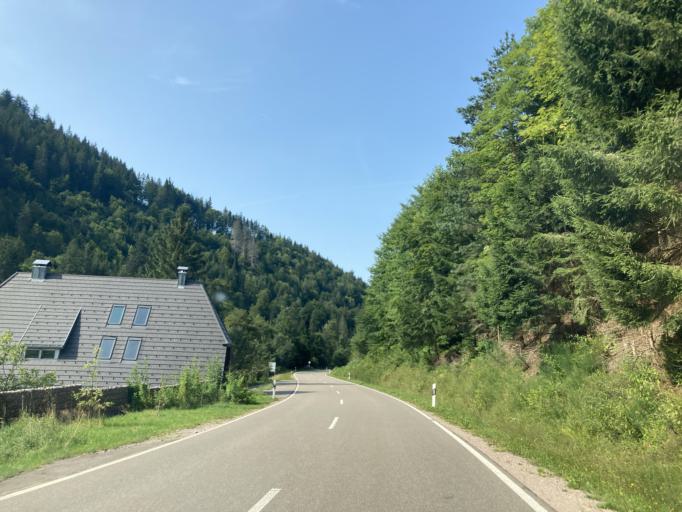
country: DE
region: Baden-Wuerttemberg
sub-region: Freiburg Region
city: Schonach im Schwarzwald
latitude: 48.1393
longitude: 8.1592
